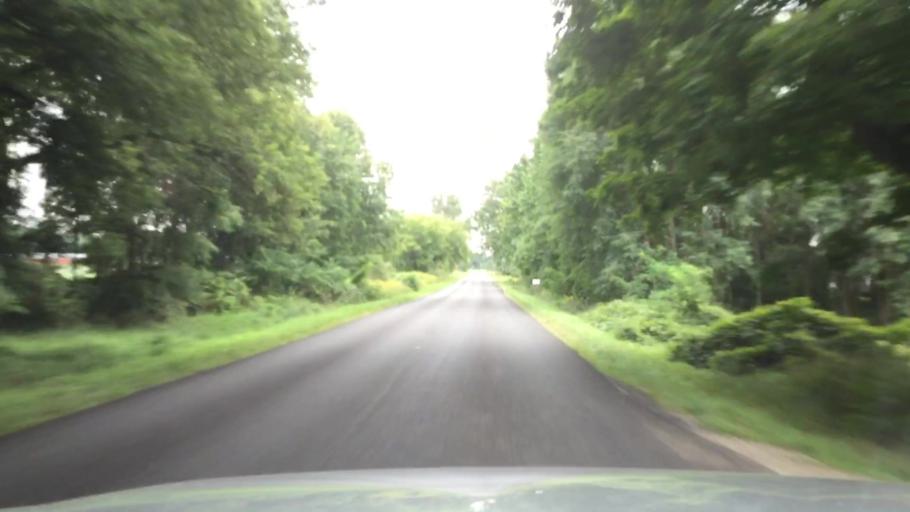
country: US
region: Michigan
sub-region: Shiawassee County
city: Durand
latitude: 42.8688
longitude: -84.0515
